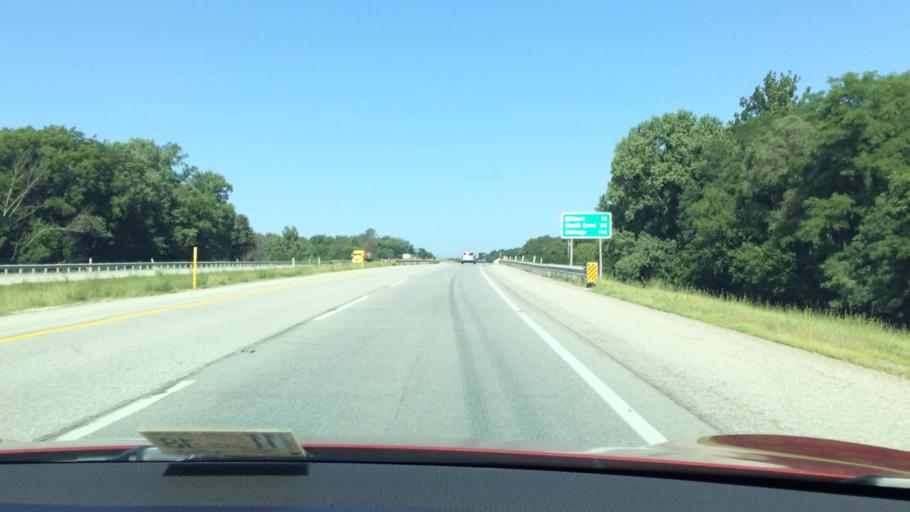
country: US
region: Indiana
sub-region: Elkhart County
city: Bristol
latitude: 41.7348
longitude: -85.8079
